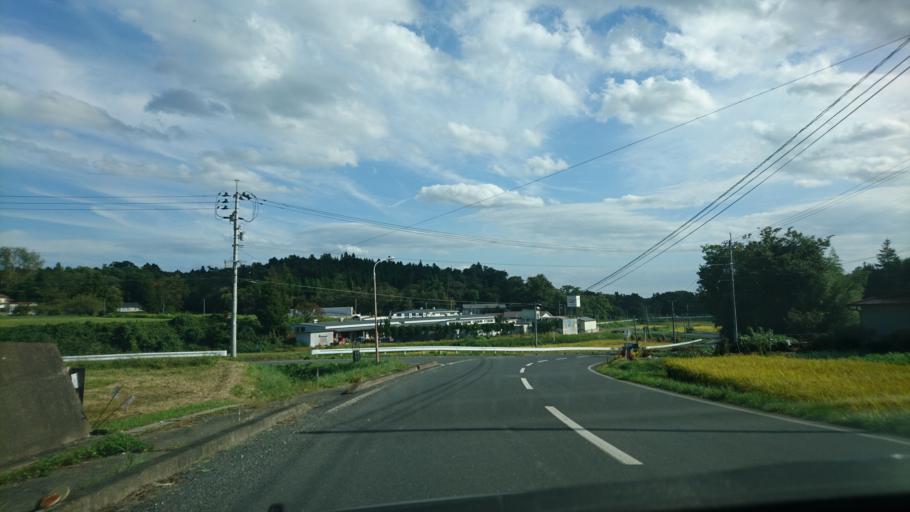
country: JP
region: Iwate
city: Ichinoseki
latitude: 38.8404
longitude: 141.1913
